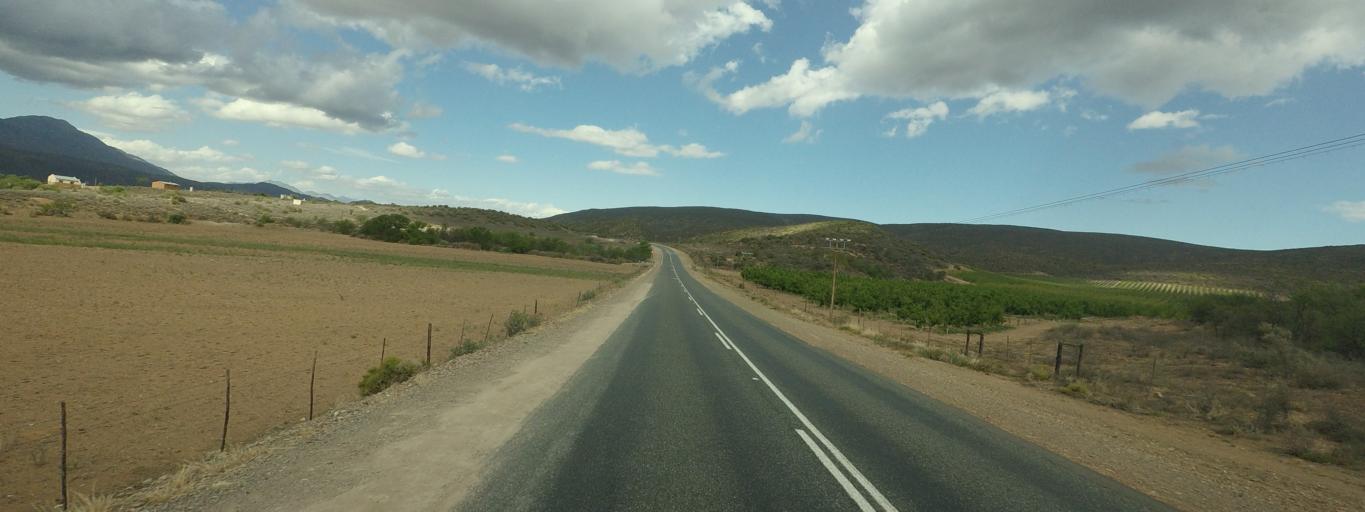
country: ZA
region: Western Cape
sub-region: Eden District Municipality
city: Ladismith
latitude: -33.5019
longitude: 21.4172
